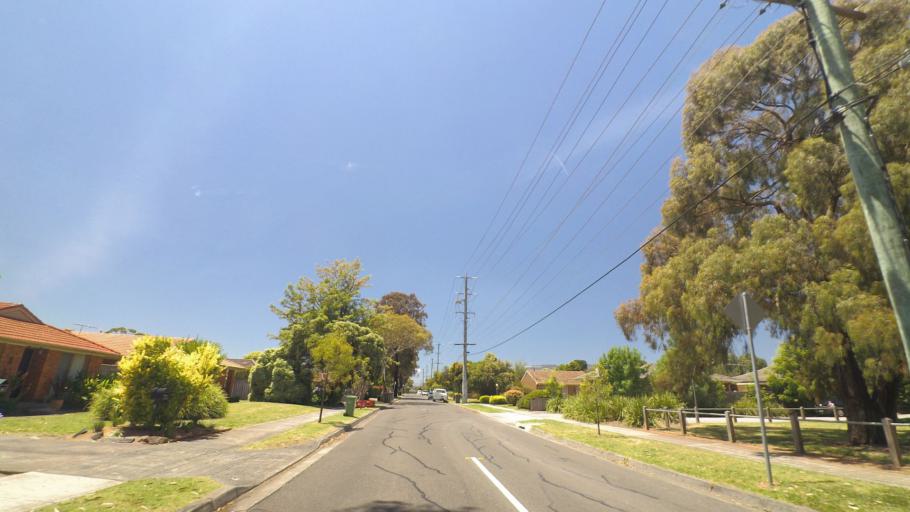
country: AU
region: Victoria
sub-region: Knox
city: Bayswater
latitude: -37.8336
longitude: 145.2740
